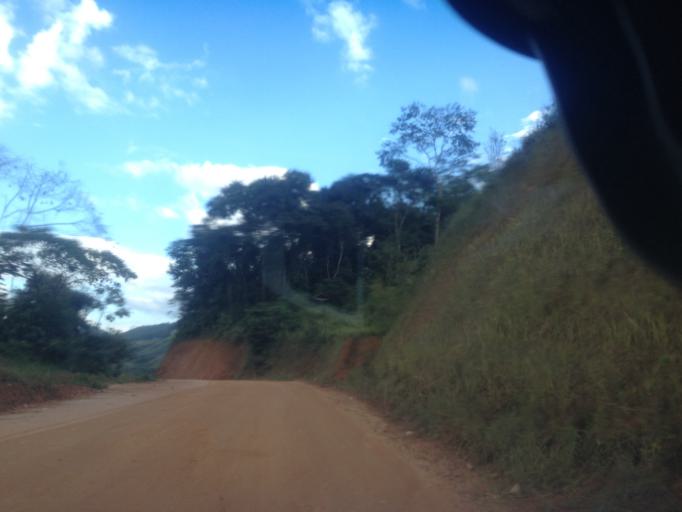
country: BR
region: Rio de Janeiro
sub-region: Quatis
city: Quatis
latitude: -22.2370
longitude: -44.2617
